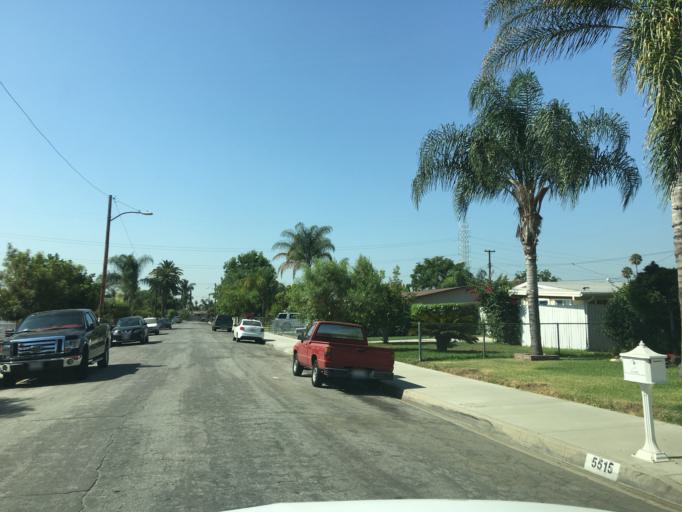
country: US
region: California
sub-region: Los Angeles County
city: Citrus
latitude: 34.1130
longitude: -117.9037
